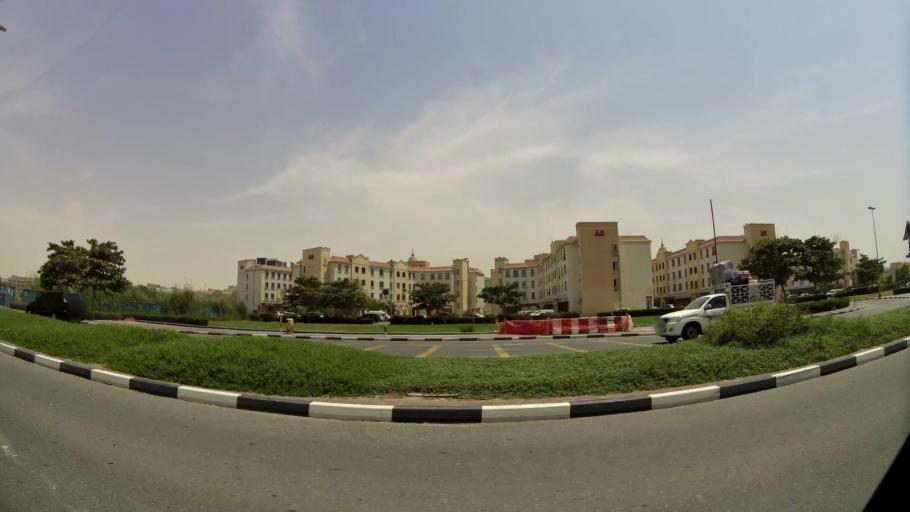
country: AE
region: Ash Shariqah
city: Sharjah
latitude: 25.1744
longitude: 55.4083
